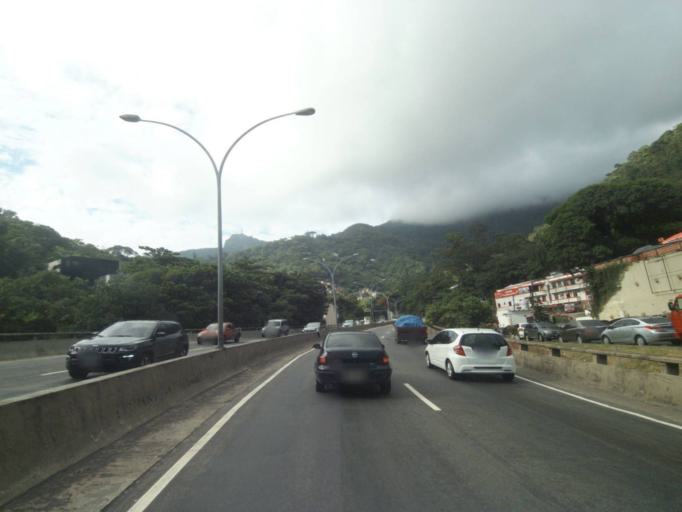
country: BR
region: Rio de Janeiro
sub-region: Rio De Janeiro
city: Rio de Janeiro
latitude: -22.9311
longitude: -43.2089
